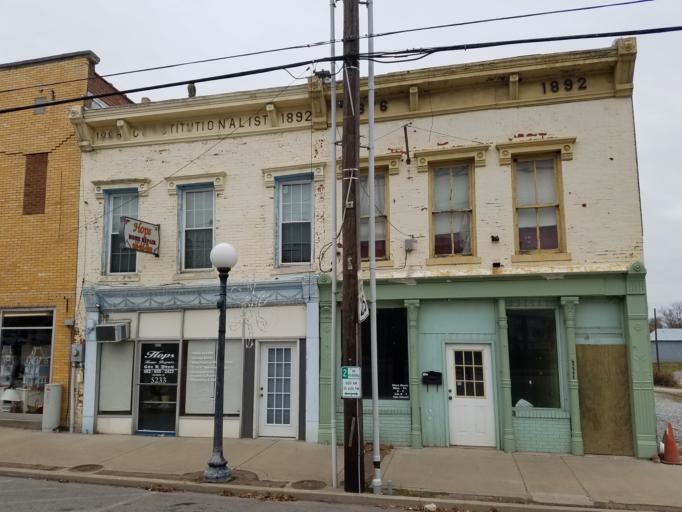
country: US
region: Kentucky
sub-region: Henry County
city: Eminence
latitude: 38.3690
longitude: -85.1803
